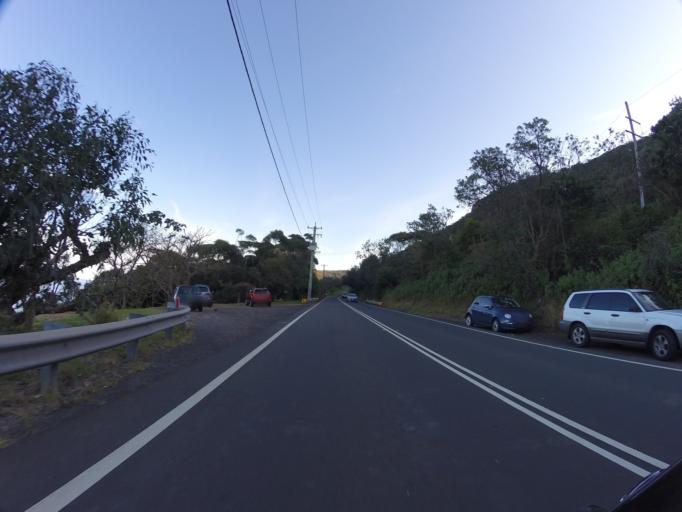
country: AU
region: New South Wales
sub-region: Wollongong
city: Helensburgh
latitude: -34.2379
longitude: 150.9836
